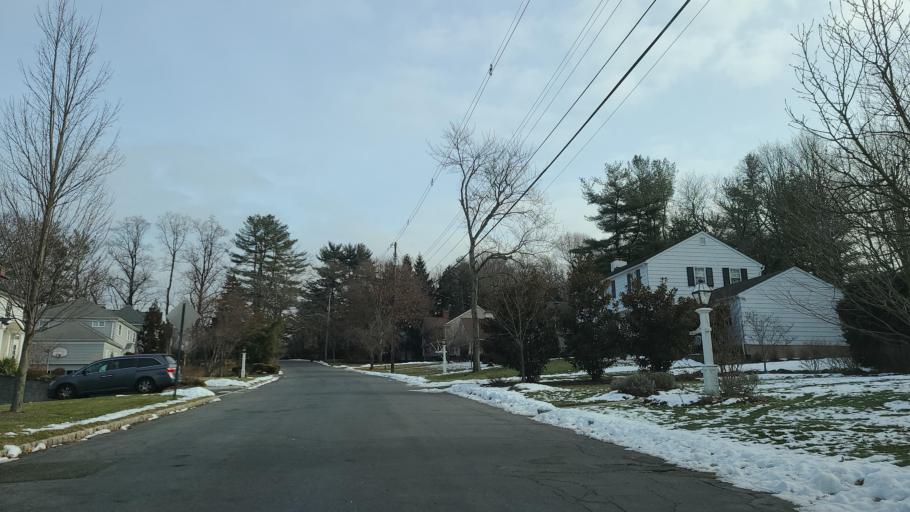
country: US
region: New Jersey
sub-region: Union County
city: Summit
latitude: 40.7340
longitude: -74.3469
